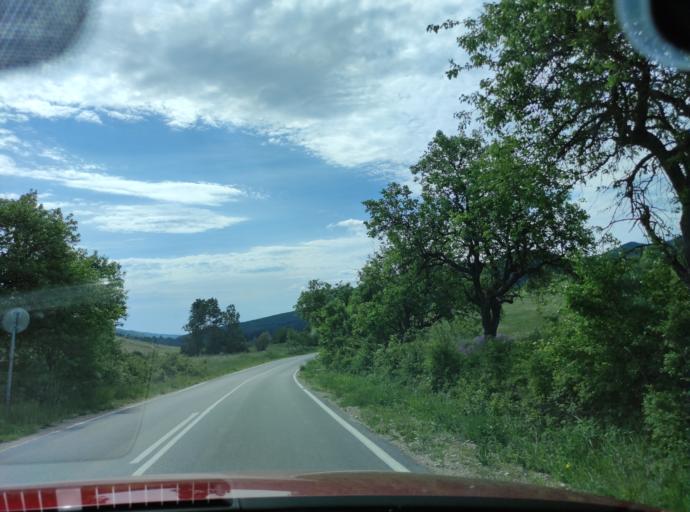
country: BG
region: Montana
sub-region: Obshtina Chiprovtsi
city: Chiprovtsi
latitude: 43.4744
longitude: 22.8448
